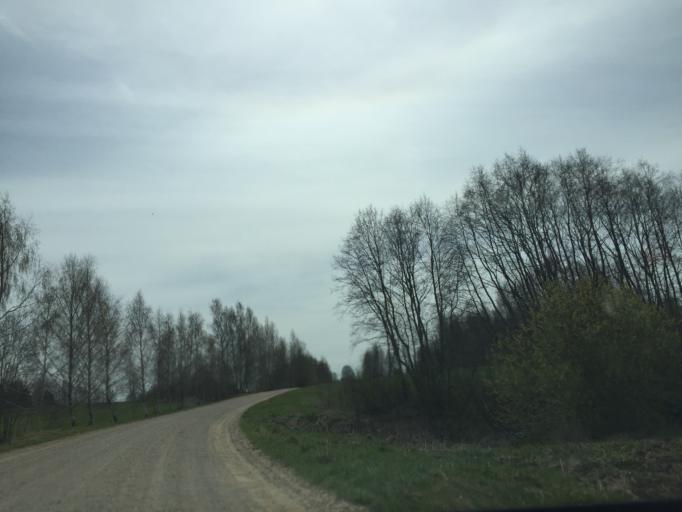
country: LV
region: Ludzas Rajons
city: Ludza
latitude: 56.5797
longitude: 27.5486
